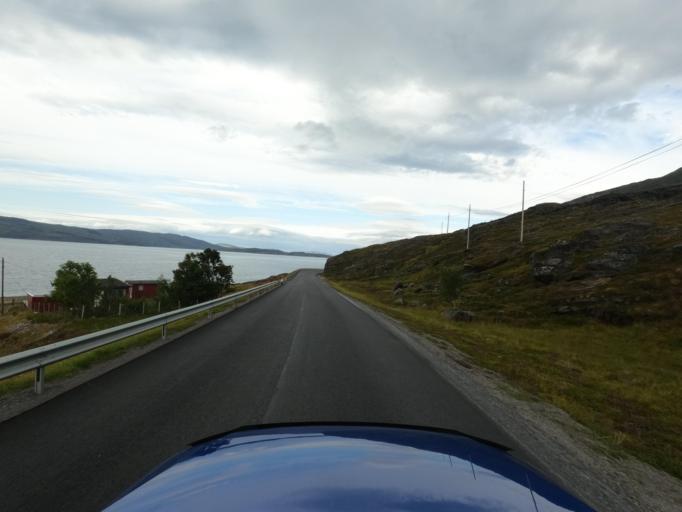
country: NO
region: Finnmark Fylke
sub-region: Hammerfest
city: Rypefjord
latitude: 70.5672
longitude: 23.6990
